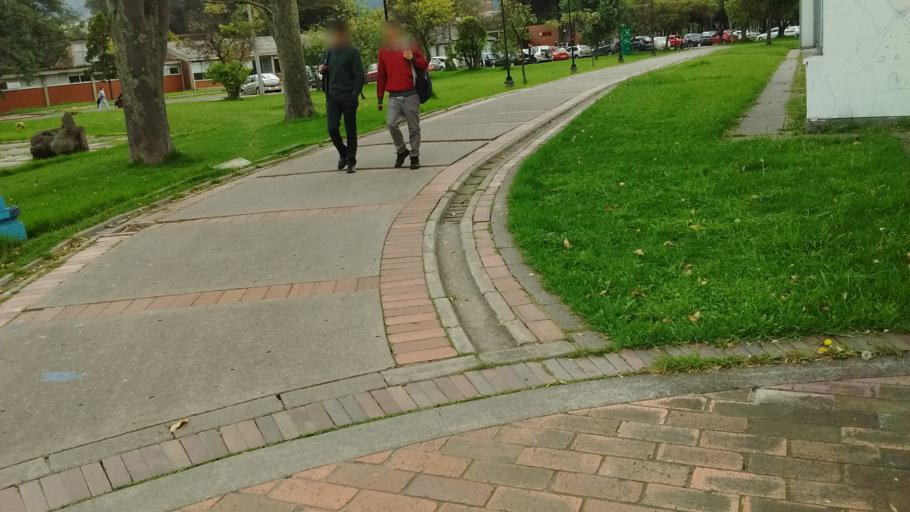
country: CO
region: Bogota D.C.
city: Bogota
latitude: 4.6363
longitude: -74.0815
